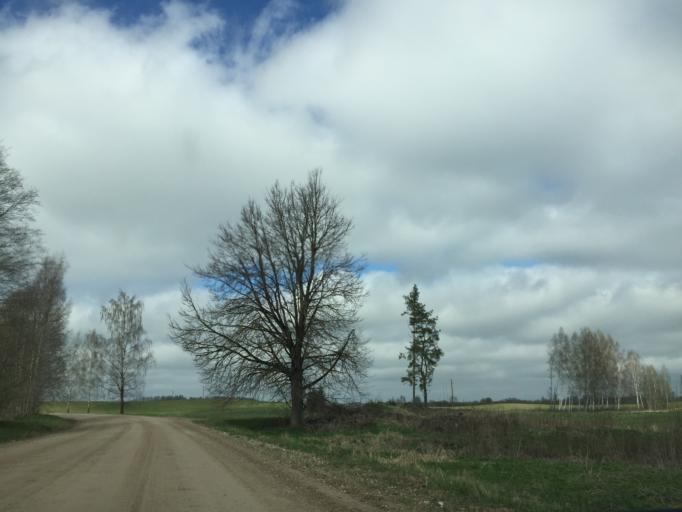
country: EE
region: Valgamaa
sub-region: Valga linn
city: Valga
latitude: 57.5428
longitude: 26.3151
